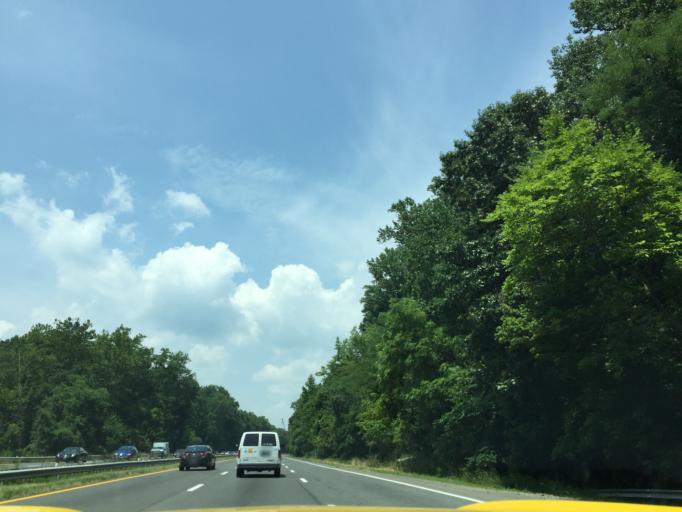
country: US
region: Maryland
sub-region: Prince George's County
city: Fort Washington
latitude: 38.7026
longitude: -76.9874
